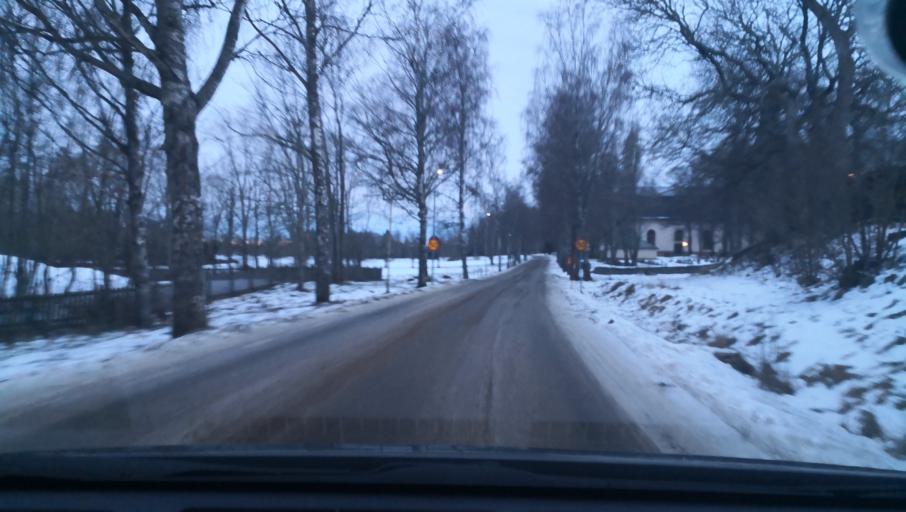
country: SE
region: Dalarna
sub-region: Avesta Kommun
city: Horndal
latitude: 60.2034
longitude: 16.4775
